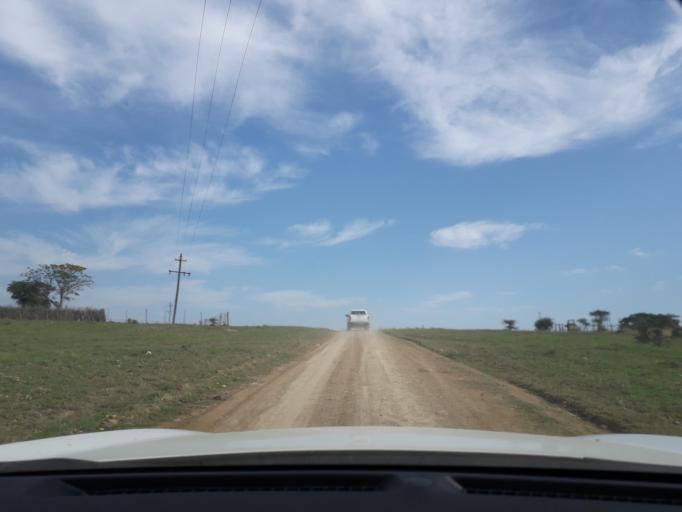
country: ZA
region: Eastern Cape
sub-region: Buffalo City Metropolitan Municipality
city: Bhisho
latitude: -32.9976
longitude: 27.3310
